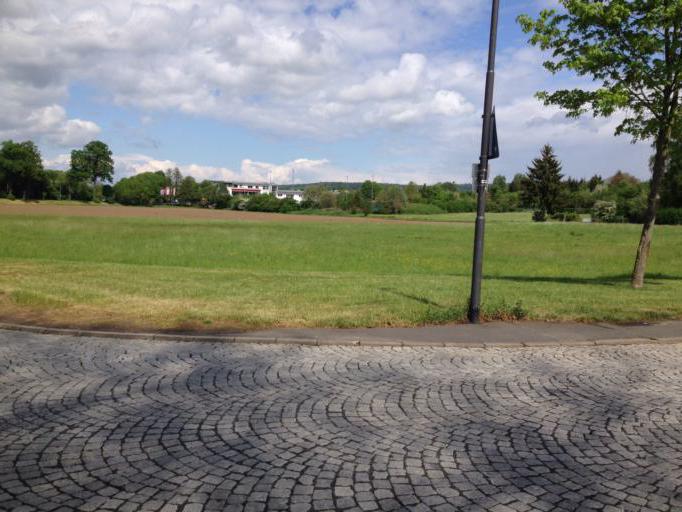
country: DE
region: Hesse
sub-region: Regierungsbezirk Giessen
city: Alsfeld
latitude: 50.7489
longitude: 9.2786
